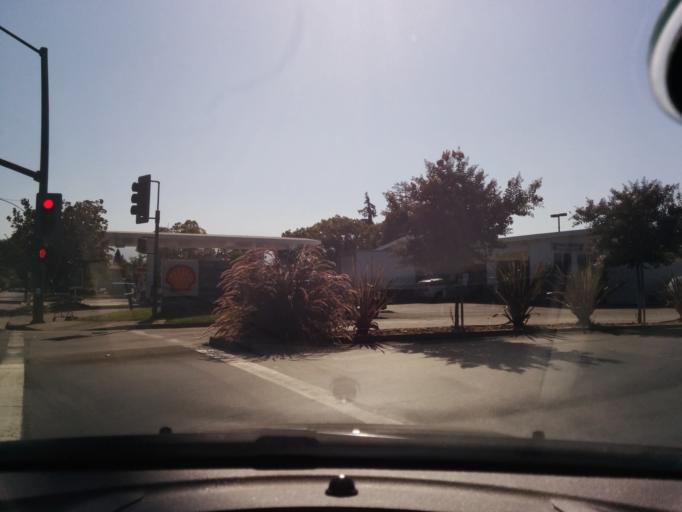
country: US
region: California
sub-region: Santa Clara County
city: Mountain View
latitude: 37.3784
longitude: -122.0748
